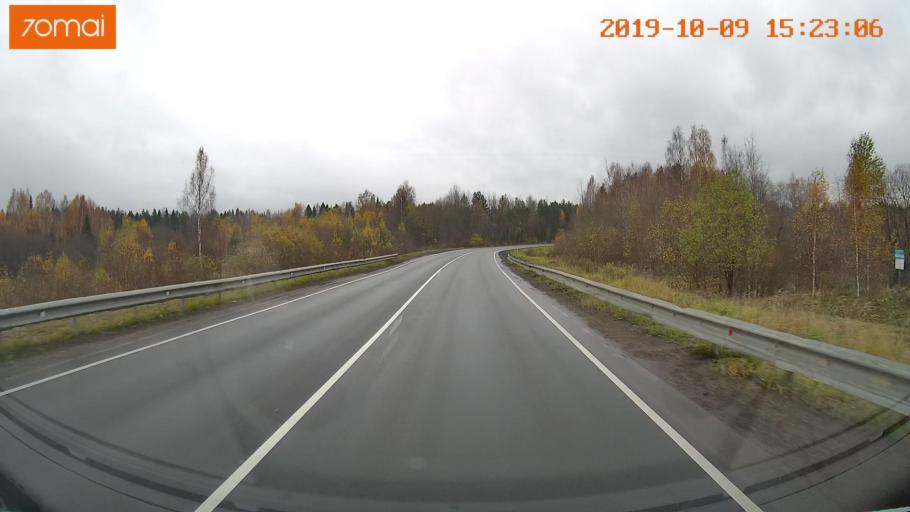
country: RU
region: Kostroma
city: Susanino
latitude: 58.0381
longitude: 41.4868
